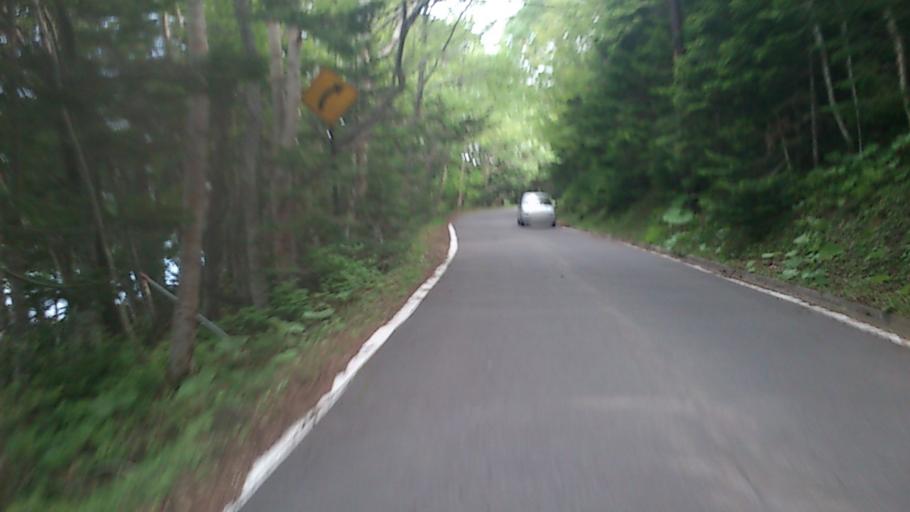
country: JP
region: Hokkaido
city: Kitami
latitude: 43.3873
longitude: 143.9685
